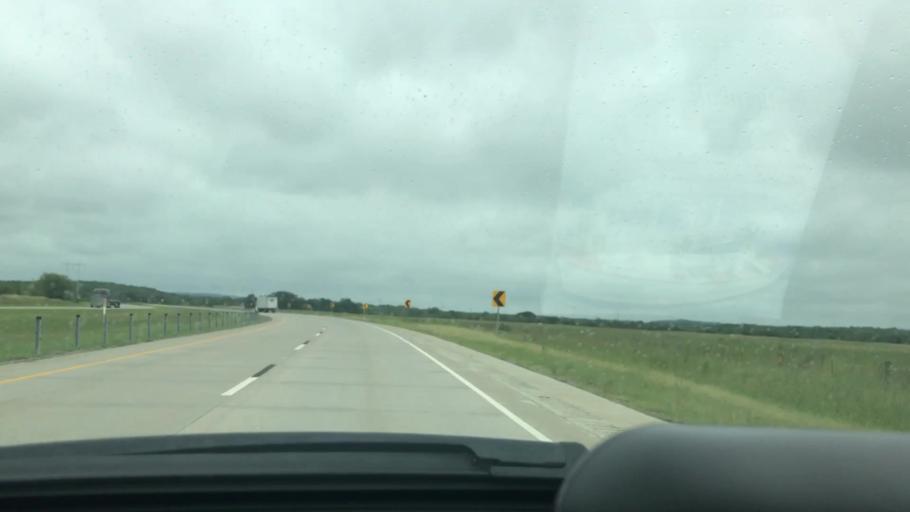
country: US
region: Oklahoma
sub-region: Pittsburg County
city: McAlester
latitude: 34.6895
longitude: -95.9146
